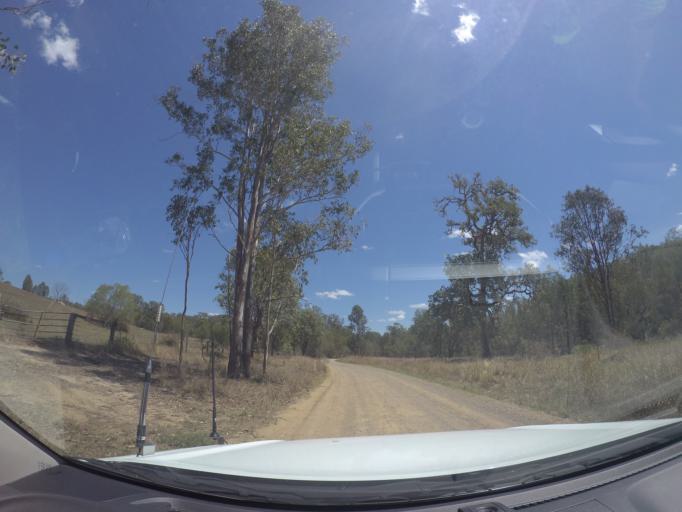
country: AU
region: Queensland
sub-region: Logan
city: North Maclean
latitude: -27.8274
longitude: 152.8634
